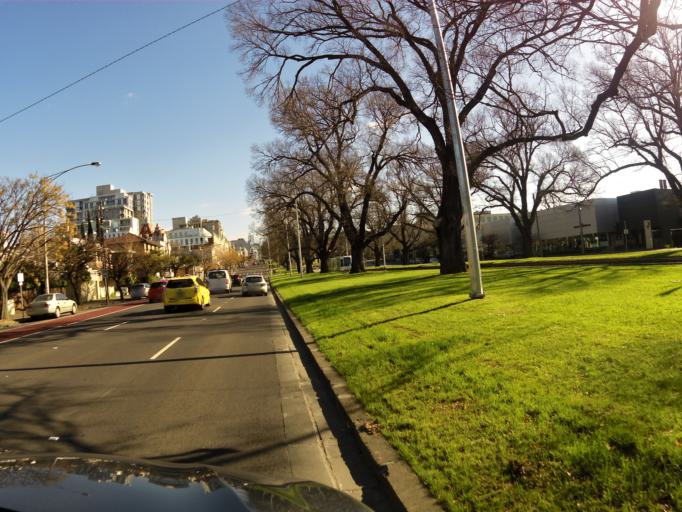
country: AU
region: Victoria
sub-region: Melbourne
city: East Melbourne
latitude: -37.8097
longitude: 144.9882
